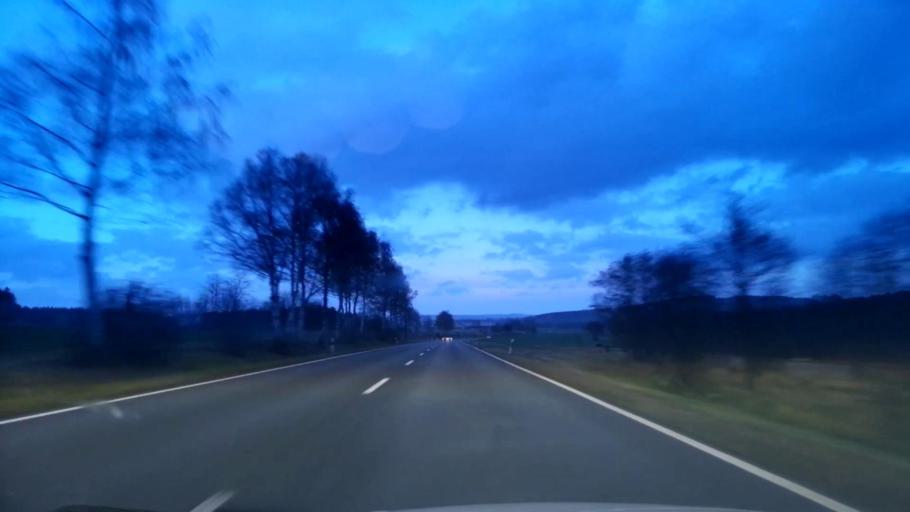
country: DE
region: Bavaria
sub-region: Upper Palatinate
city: Waldershof
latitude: 49.9653
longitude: 12.0934
